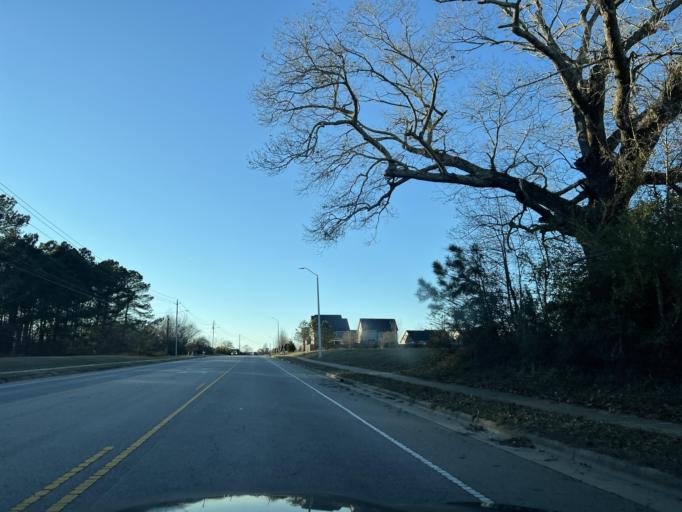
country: US
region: North Carolina
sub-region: Wake County
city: Fuquay-Varina
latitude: 35.5737
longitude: -78.8033
